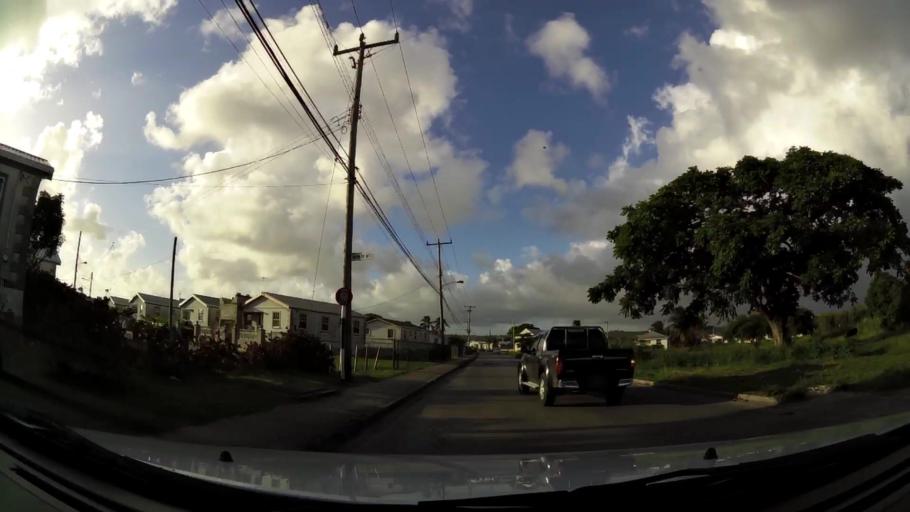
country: BB
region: Saint Philip
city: Crane
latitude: 13.1123
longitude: -59.4732
